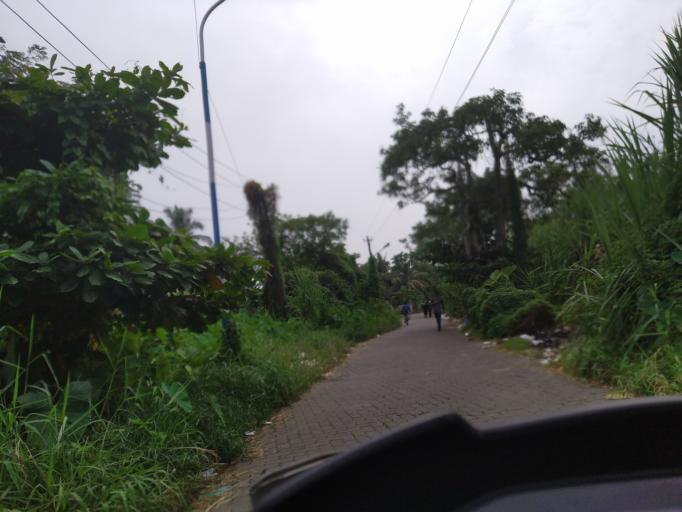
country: IN
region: Kerala
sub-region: Ernakulam
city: Cochin
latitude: 9.9513
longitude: 76.2944
